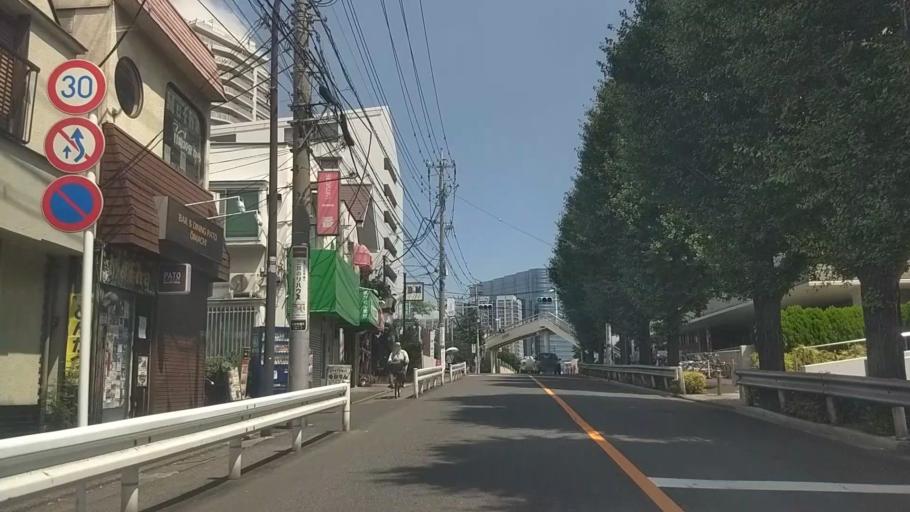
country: JP
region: Kanagawa
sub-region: Kawasaki-shi
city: Kawasaki
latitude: 35.6086
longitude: 139.7296
